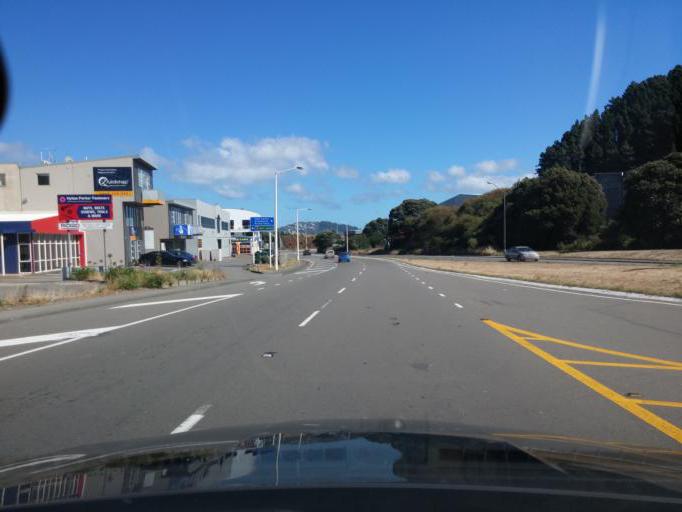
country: NZ
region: Wellington
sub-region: Wellington City
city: Wellington
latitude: -41.2448
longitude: 174.8140
